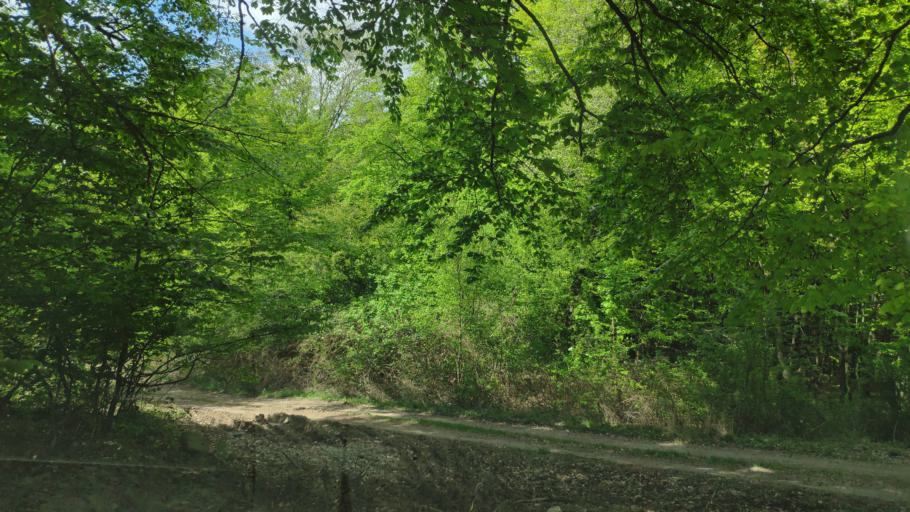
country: SK
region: Kosicky
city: Kosice
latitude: 48.6732
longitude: 21.4496
